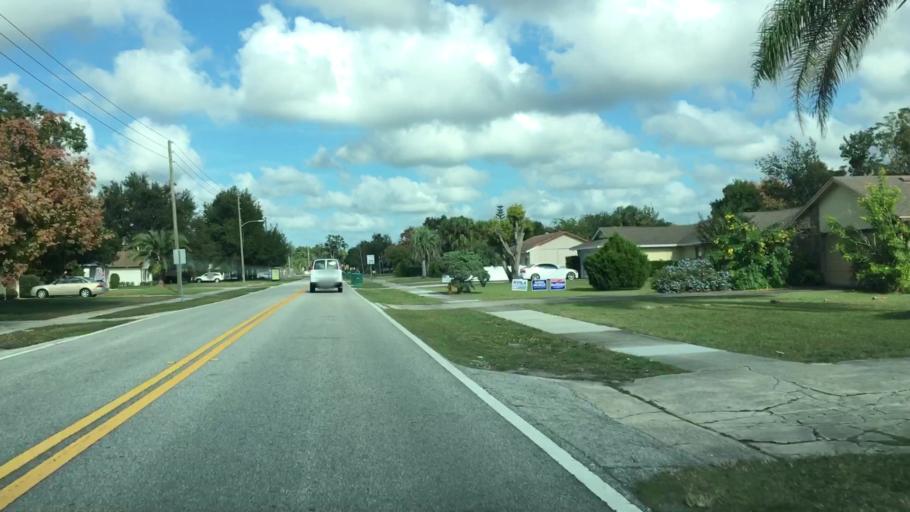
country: US
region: Florida
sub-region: Volusia County
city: Deltona
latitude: 28.8892
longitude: -81.2451
